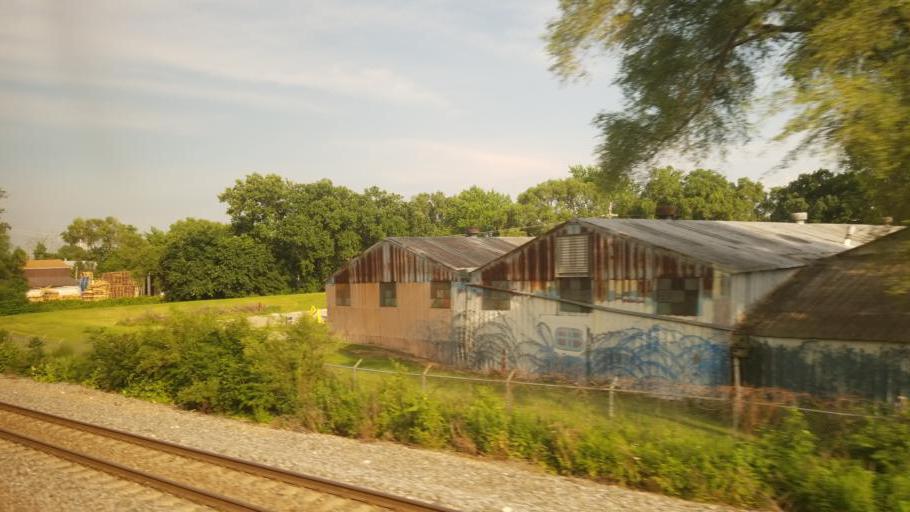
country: US
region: Illinois
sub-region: Kane County
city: Aurora
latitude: 41.7686
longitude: -88.2853
